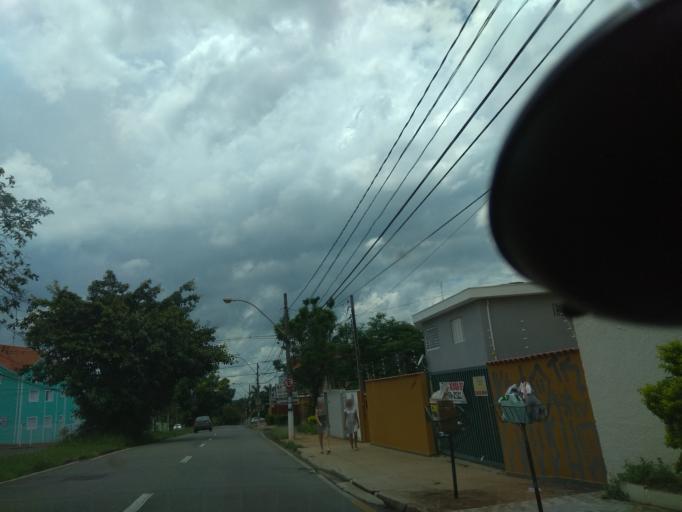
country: BR
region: Sao Paulo
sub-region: Campinas
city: Campinas
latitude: -22.8250
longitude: -47.0717
